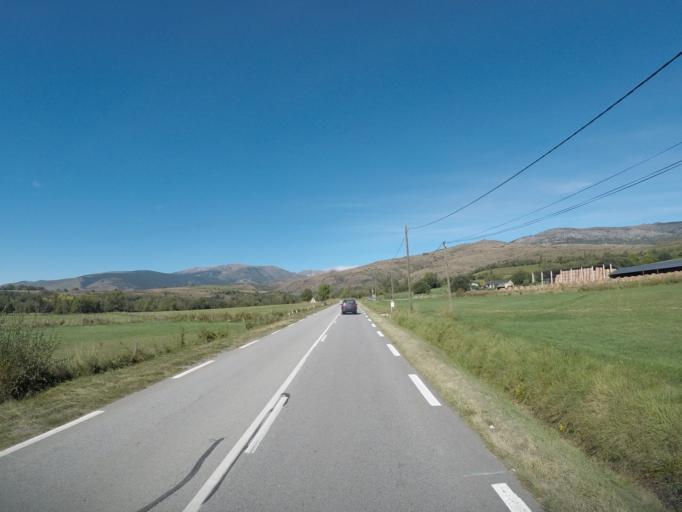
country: FR
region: Languedoc-Roussillon
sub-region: Departement des Pyrenees-Orientales
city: la Guingueta d'Ix
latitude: 42.4570
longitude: 1.9504
